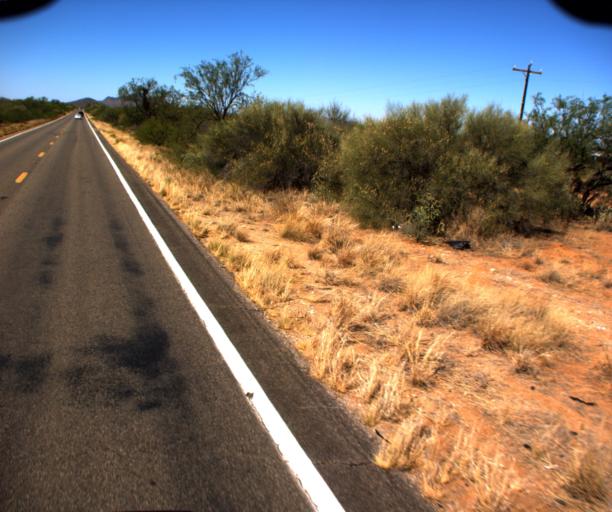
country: US
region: Arizona
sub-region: Pima County
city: Sells
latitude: 31.9475
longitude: -111.7645
